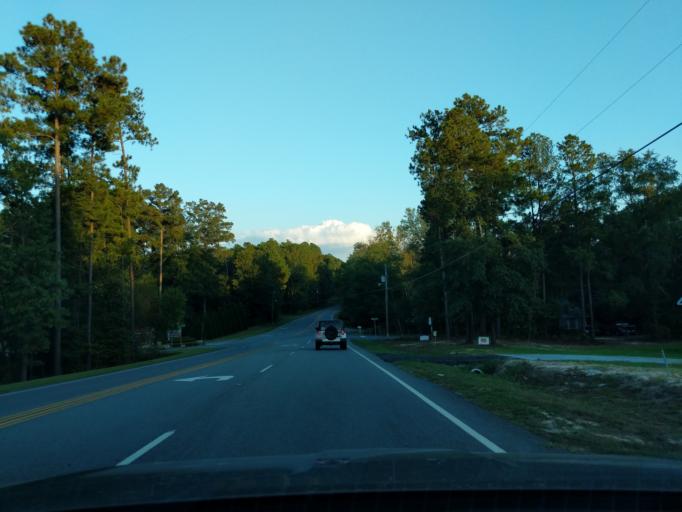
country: US
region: South Carolina
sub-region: Aiken County
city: Burnettown
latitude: 33.5295
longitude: -81.8571
